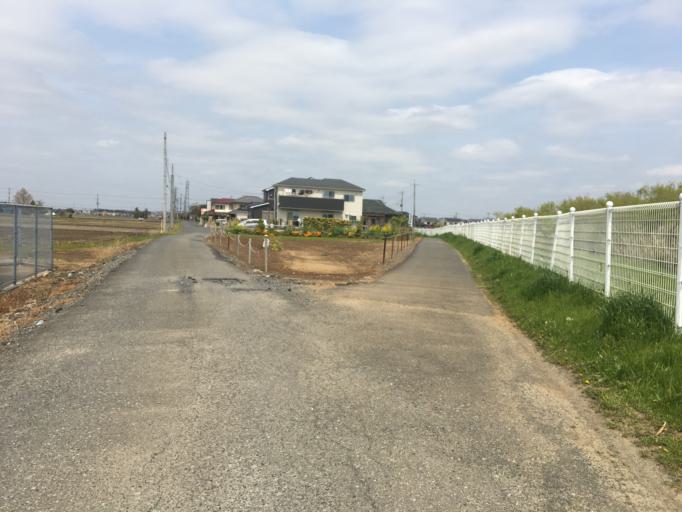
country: JP
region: Saitama
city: Kamifukuoka
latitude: 35.8874
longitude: 139.5485
